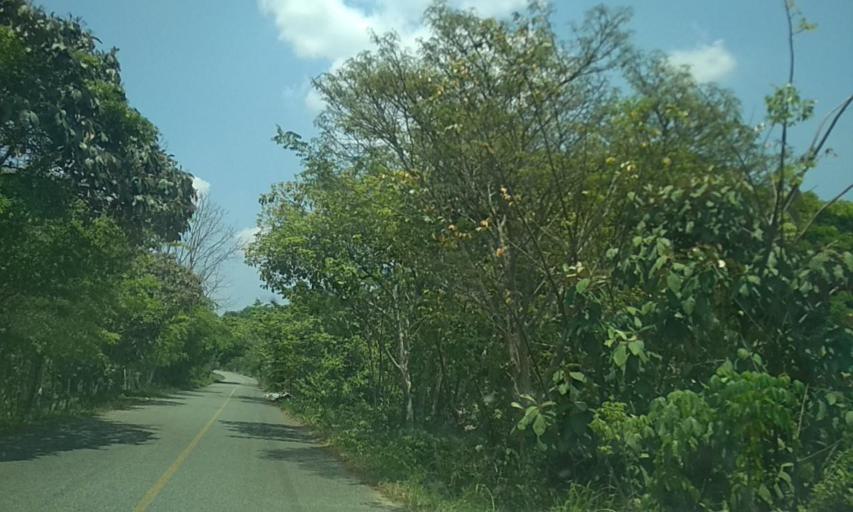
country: MX
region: Tabasco
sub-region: Huimanguillo
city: Francisco Rueda
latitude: 17.8363
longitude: -93.9140
